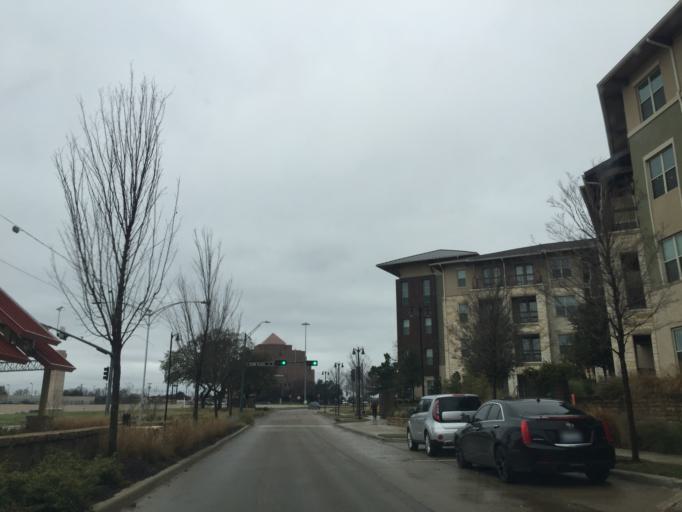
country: US
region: Texas
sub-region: Tarrant County
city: Arlington
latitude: 32.7609
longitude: -97.1101
